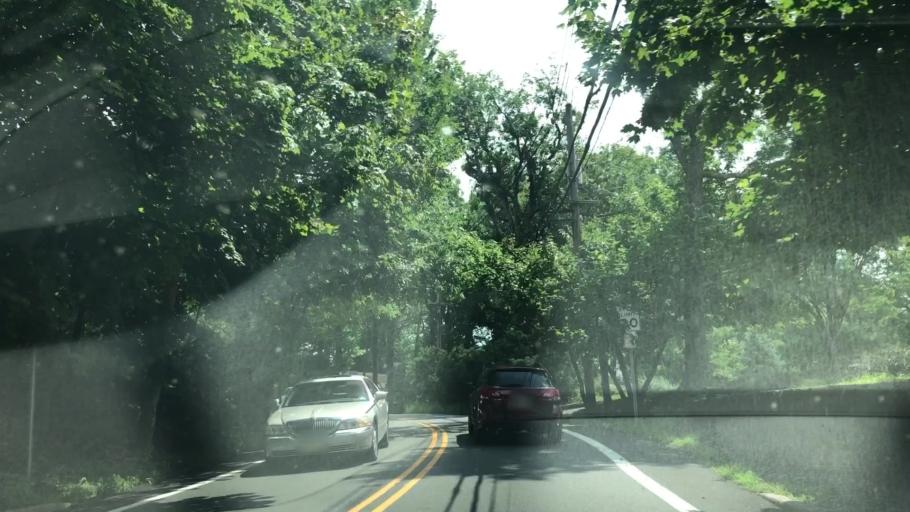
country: US
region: New Jersey
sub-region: Passaic County
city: Little Falls
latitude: 40.8675
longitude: -74.2052
